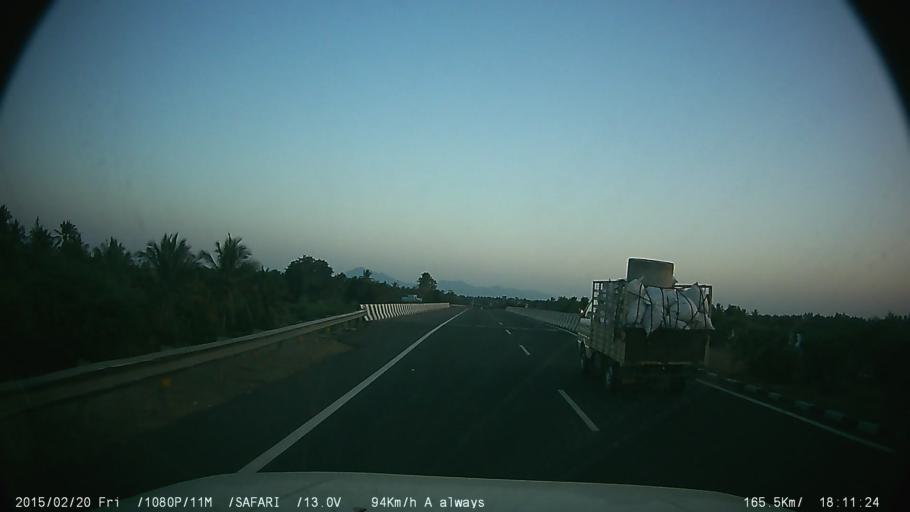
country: IN
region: Tamil Nadu
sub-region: Dharmapuri
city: Palakkodu
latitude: 12.2642
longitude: 78.1966
